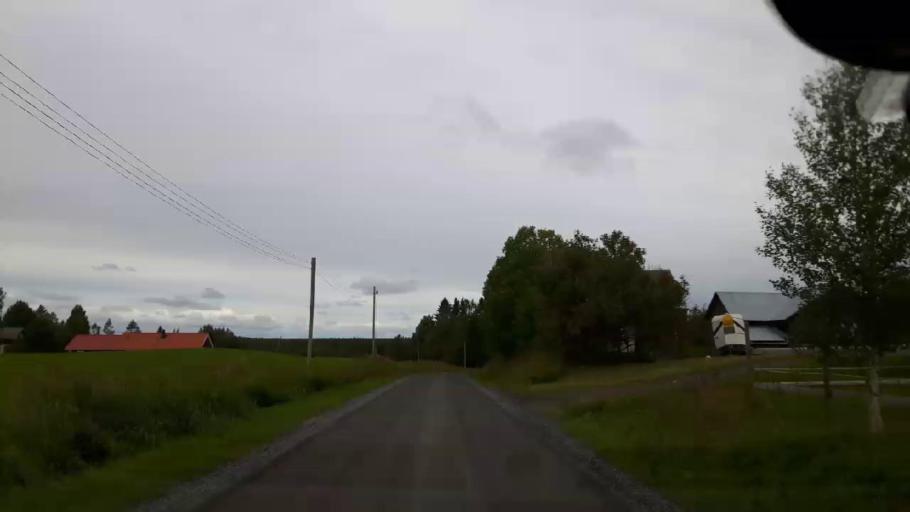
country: SE
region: Jaemtland
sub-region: Krokoms Kommun
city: Krokom
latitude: 63.2695
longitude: 14.4057
